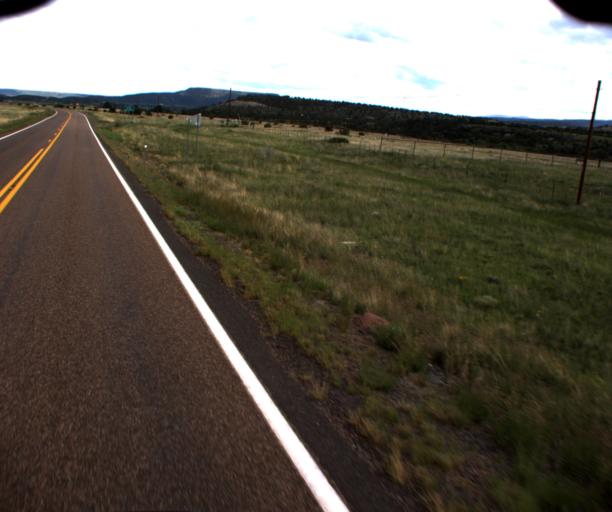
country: US
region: Arizona
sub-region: Apache County
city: Eagar
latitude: 34.1043
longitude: -109.3521
